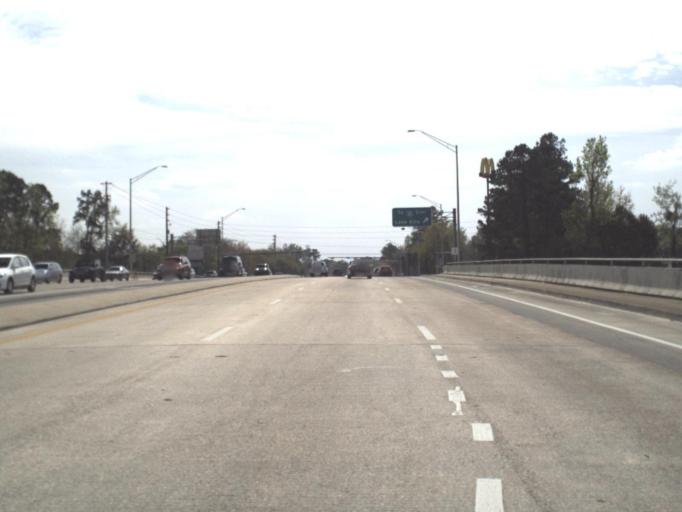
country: US
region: Florida
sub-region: Leon County
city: Tallahassee
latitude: 30.5023
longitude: -84.2484
